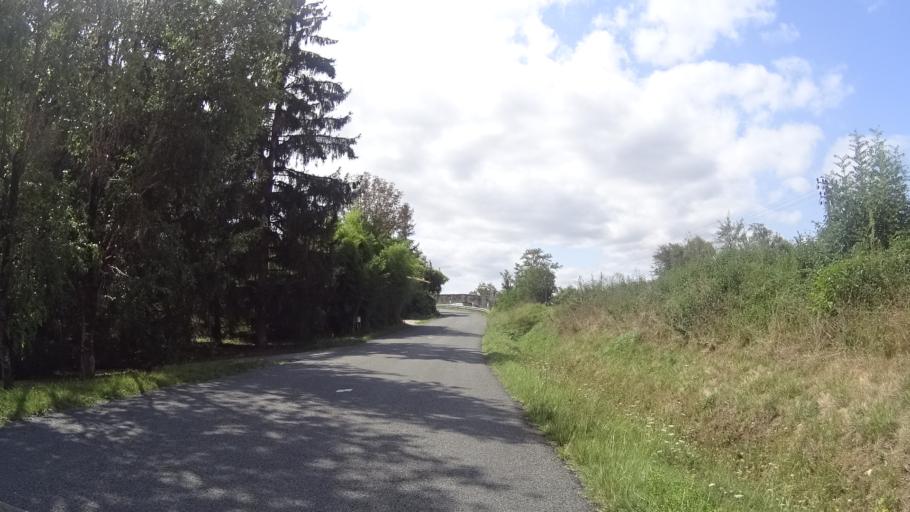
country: FR
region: Aquitaine
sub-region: Departement du Lot-et-Garonne
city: Pont-du-Casse
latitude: 44.2546
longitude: 0.6938
